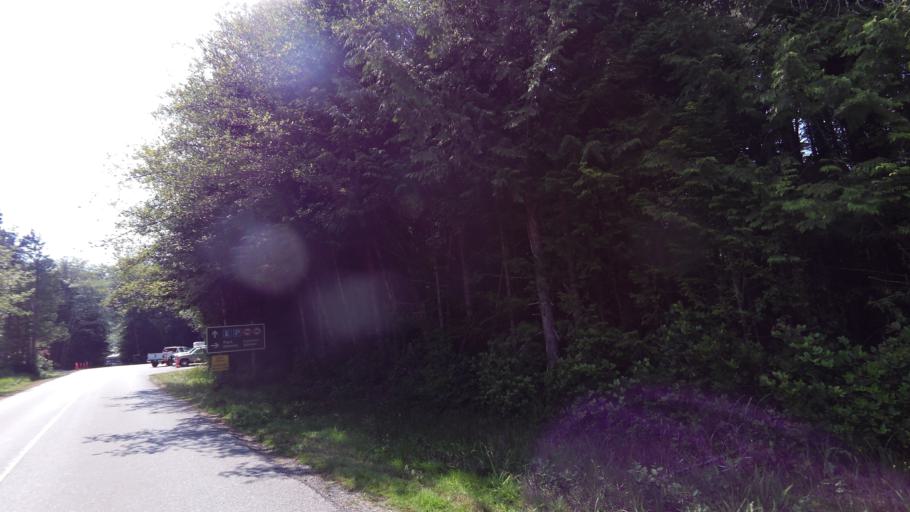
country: CA
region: British Columbia
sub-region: Regional District of Alberni-Clayoquot
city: Tofino
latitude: 49.0903
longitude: -125.8332
